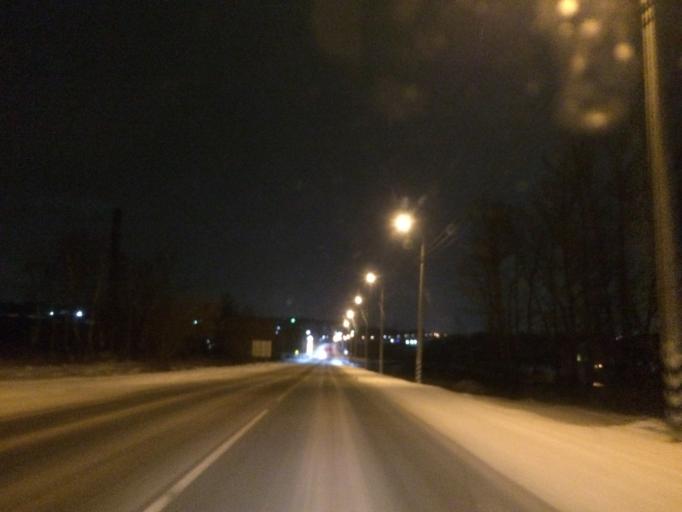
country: RU
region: Tula
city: Tula
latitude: 54.2310
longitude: 37.6555
